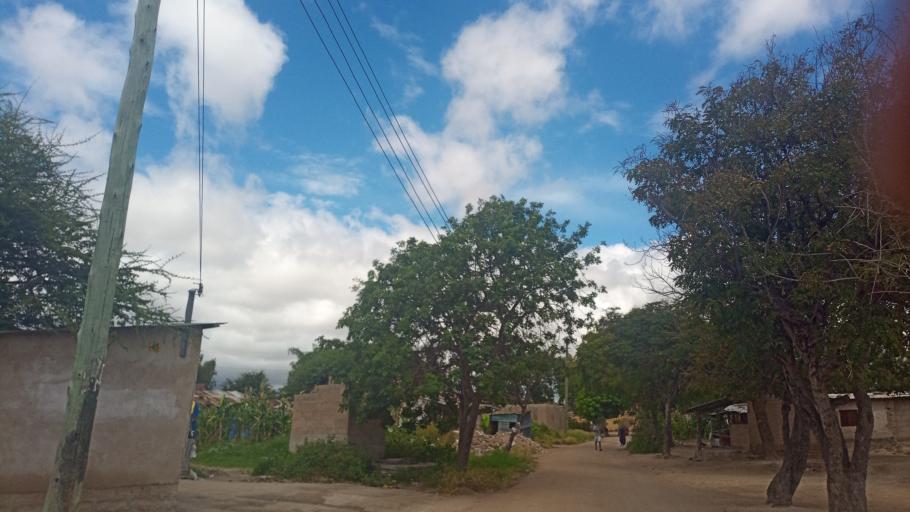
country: TZ
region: Dodoma
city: Dodoma
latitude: -6.1878
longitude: 35.7260
